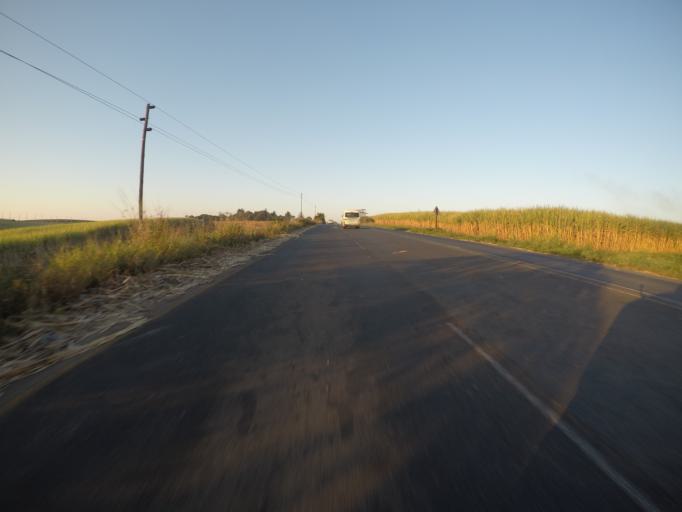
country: ZA
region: KwaZulu-Natal
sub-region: uThungulu District Municipality
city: Empangeni
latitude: -28.7893
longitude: 31.8973
